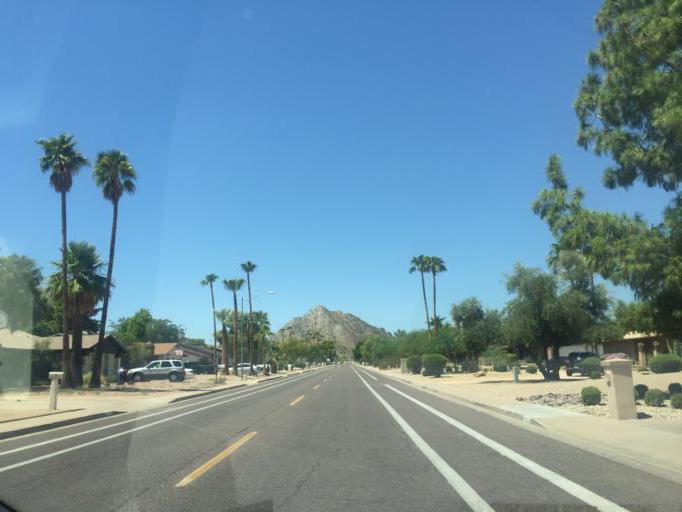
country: US
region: Arizona
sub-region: Maricopa County
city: Paradise Valley
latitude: 33.5896
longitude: -112.0239
